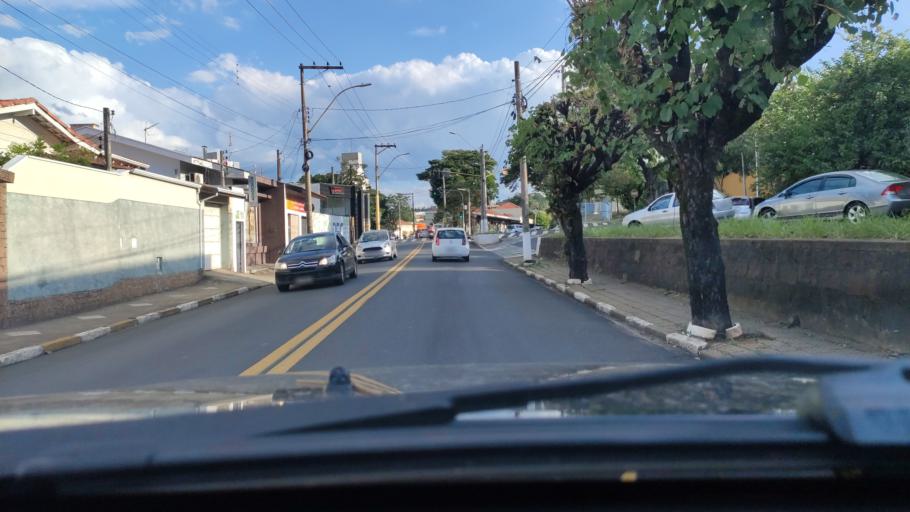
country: BR
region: Sao Paulo
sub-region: Itapira
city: Itapira
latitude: -22.4360
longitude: -46.8253
